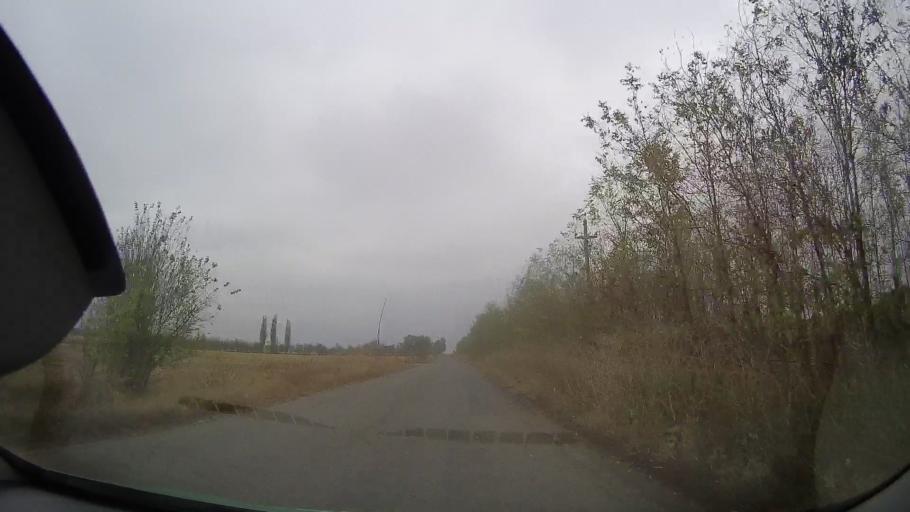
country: RO
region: Buzau
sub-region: Comuna Glodeanu-Silistea
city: Glodeanu-Silistea
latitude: 44.8124
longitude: 26.8515
